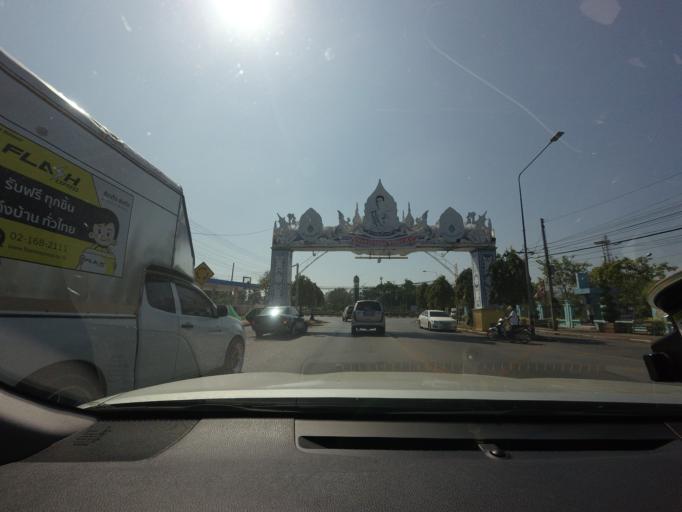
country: TH
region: Yala
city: Yala
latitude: 6.5485
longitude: 101.2841
